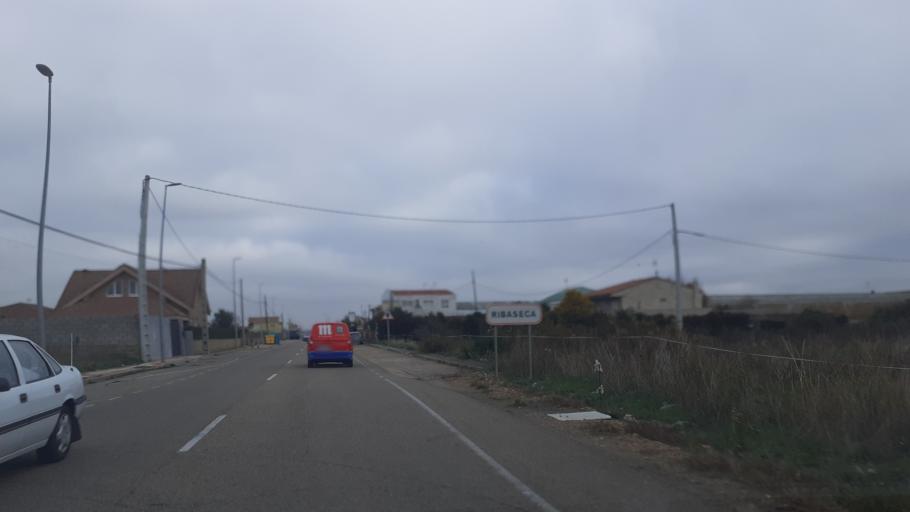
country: ES
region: Castille and Leon
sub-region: Provincia de Leon
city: Onzonilla
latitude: 42.5347
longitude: -5.5920
